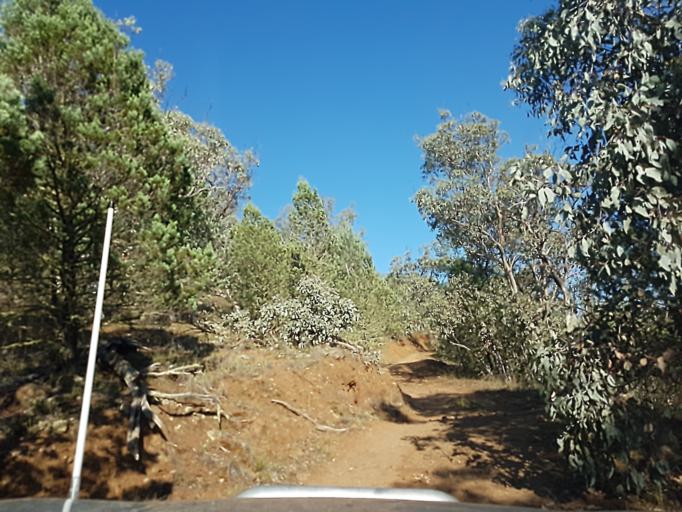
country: AU
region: New South Wales
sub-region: Snowy River
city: Jindabyne
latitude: -36.9573
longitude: 148.3785
